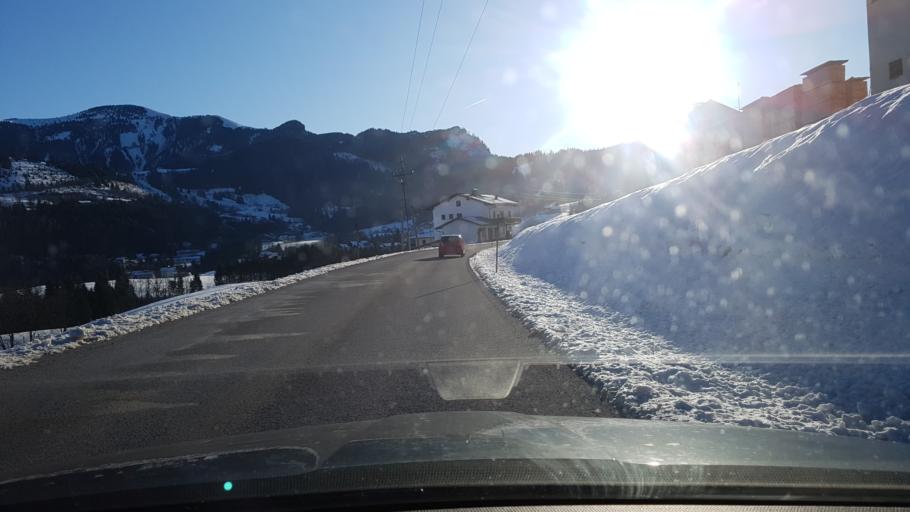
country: AT
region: Salzburg
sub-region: Politischer Bezirk Hallein
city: Golling an der Salzach
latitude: 47.6532
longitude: 13.2046
